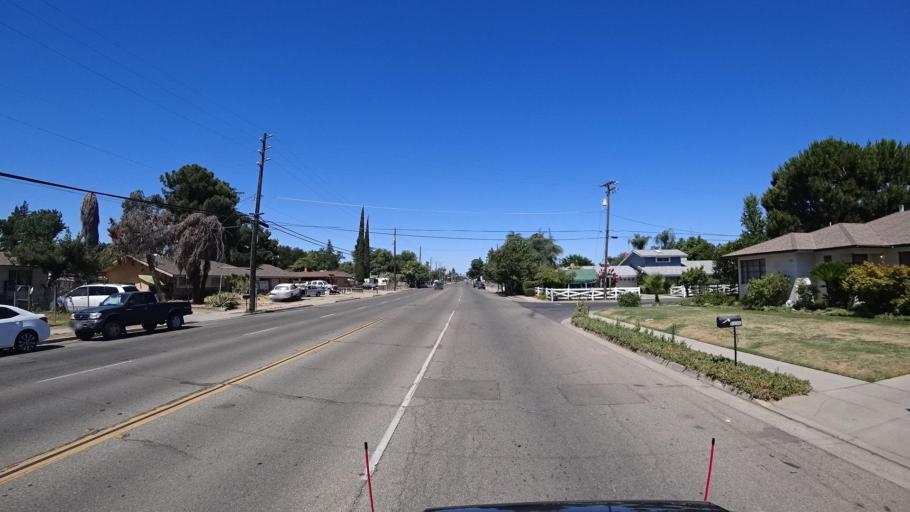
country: US
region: California
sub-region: Fresno County
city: Sunnyside
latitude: 36.7432
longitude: -119.7147
